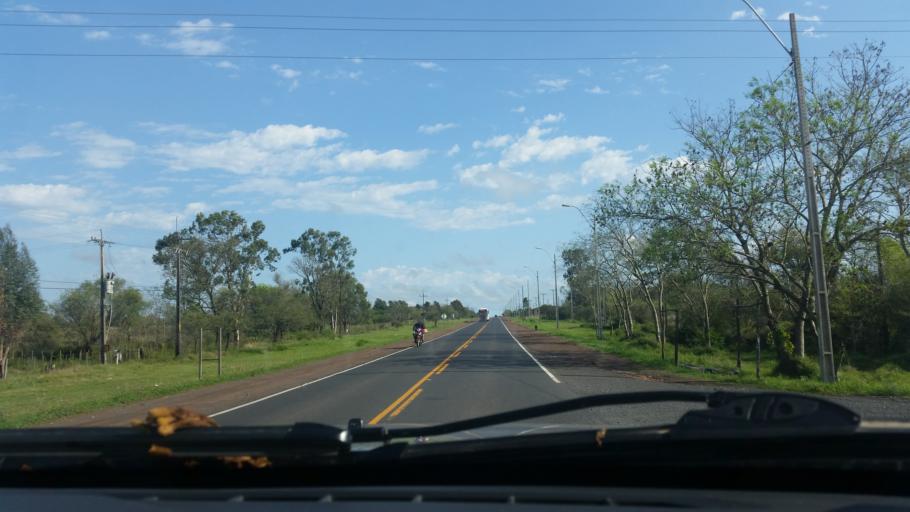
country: PY
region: Presidente Hayes
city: Villa Hayes
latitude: -25.0557
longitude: -57.5369
